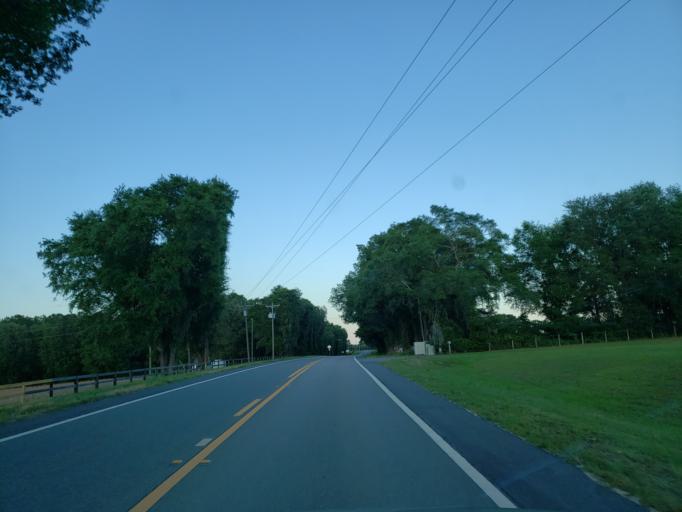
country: US
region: Georgia
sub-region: Echols County
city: Statenville
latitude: 30.5813
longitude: -83.1998
